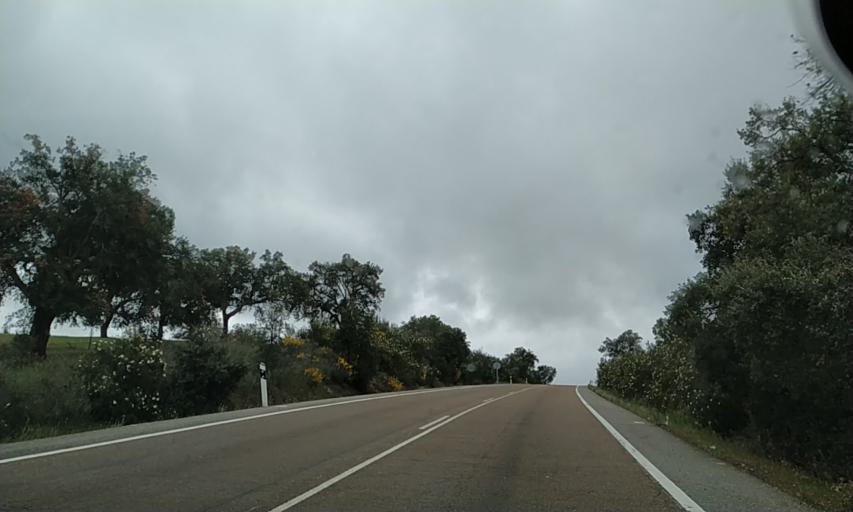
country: ES
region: Extremadura
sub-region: Provincia de Badajoz
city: Puebla de Obando
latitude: 39.2366
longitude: -6.5650
